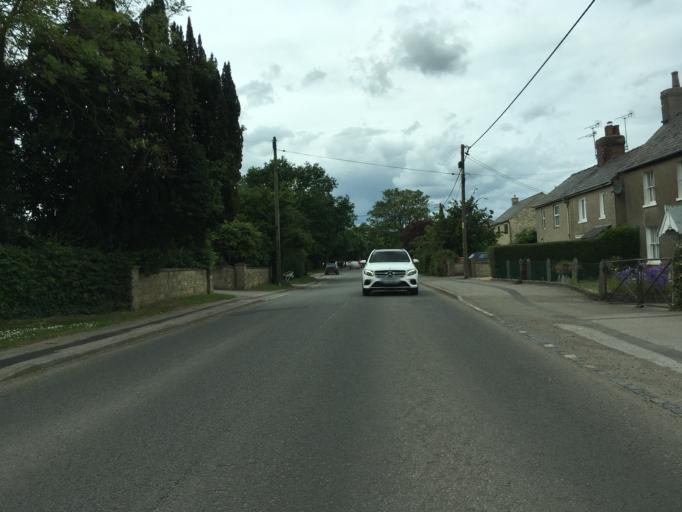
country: GB
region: England
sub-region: Wiltshire
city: Lyneham
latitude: 51.5593
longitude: -1.9796
